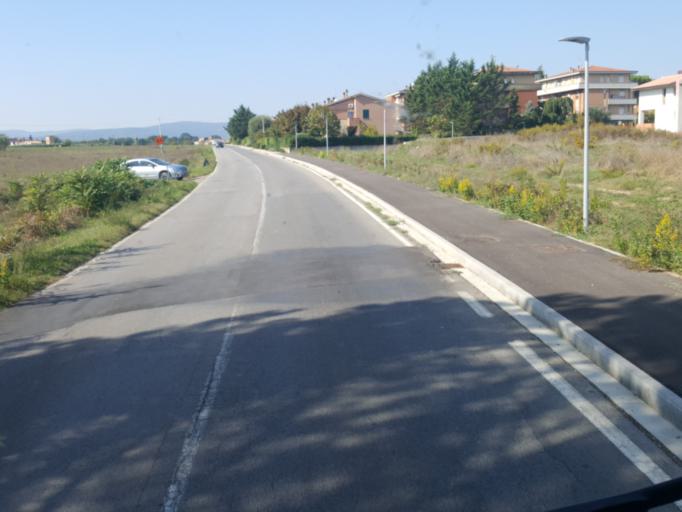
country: IT
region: Tuscany
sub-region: Provincia di Siena
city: Colle di Val d'Elsa
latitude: 43.4161
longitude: 11.1018
